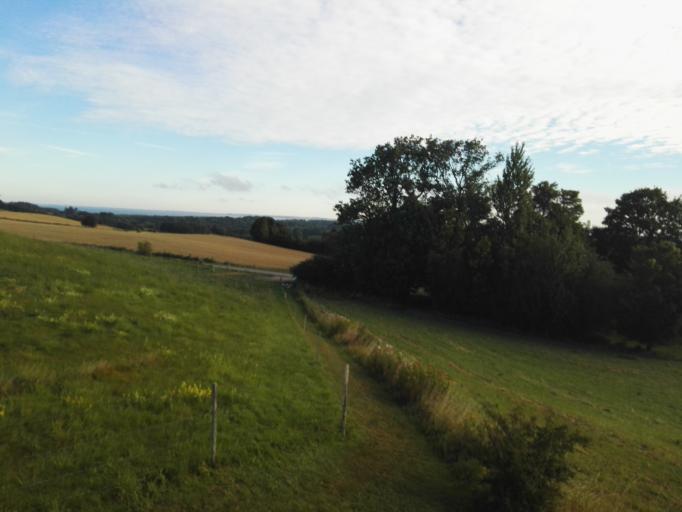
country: DK
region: Zealand
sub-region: Odsherred Kommune
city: Asnaes
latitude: 55.8223
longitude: 11.5370
